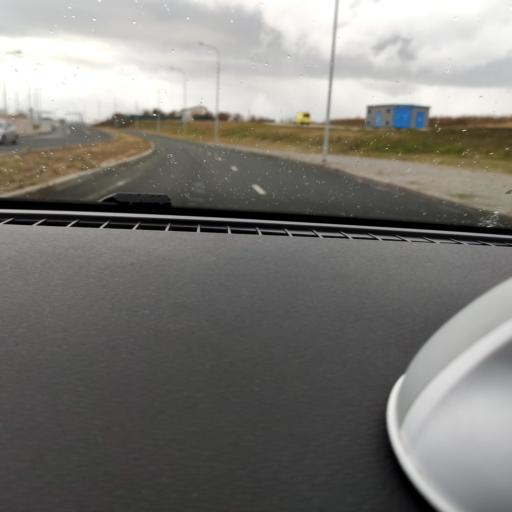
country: RU
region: Samara
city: Samara
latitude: 53.2808
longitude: 50.2350
